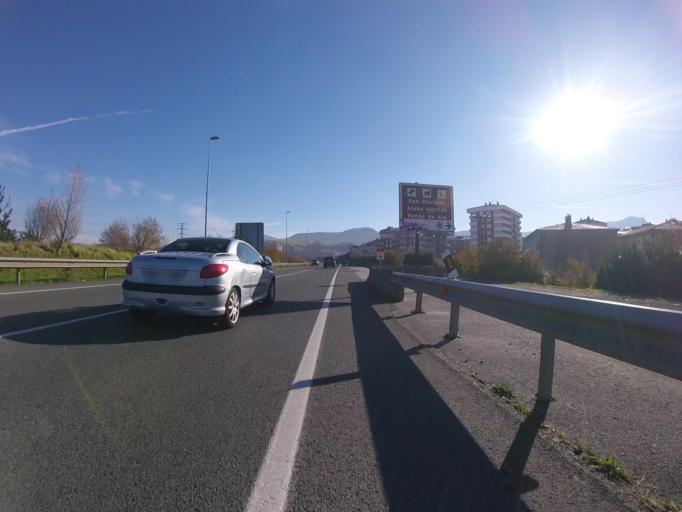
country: ES
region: Basque Country
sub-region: Provincia de Guipuzcoa
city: Irun
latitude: 43.3425
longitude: -1.7844
